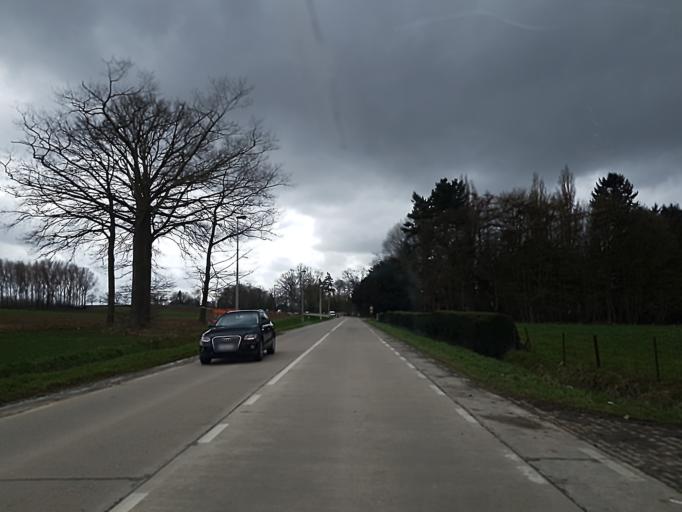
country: BE
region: Wallonia
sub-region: Province du Brabant Wallon
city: Jodoigne
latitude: 50.7070
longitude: 4.8535
